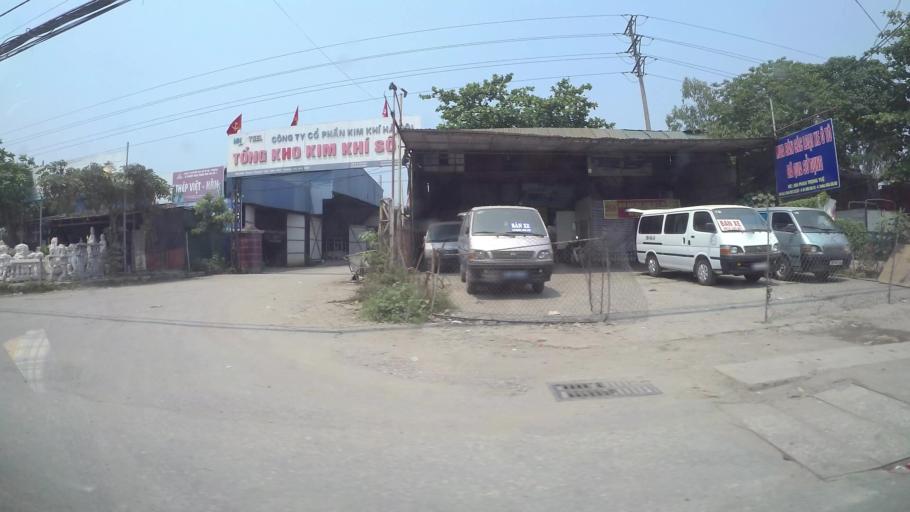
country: VN
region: Ha Noi
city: Van Dien
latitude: 20.9515
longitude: 105.8189
